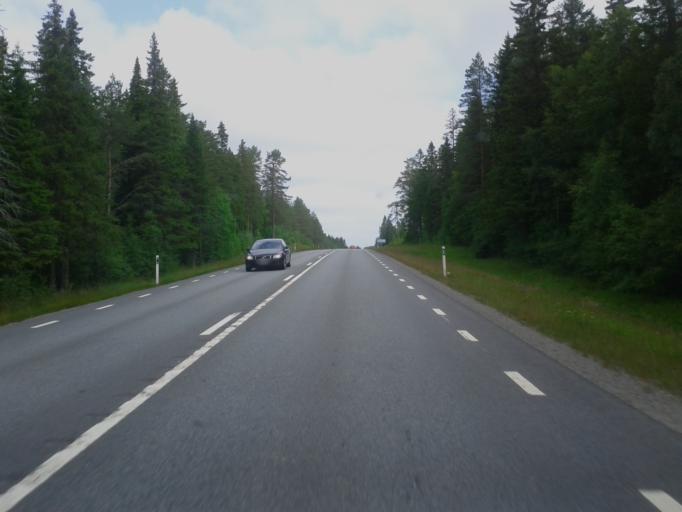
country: SE
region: Vaesterbotten
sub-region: Skelleftea Kommun
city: Burea
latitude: 64.3579
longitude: 21.2957
